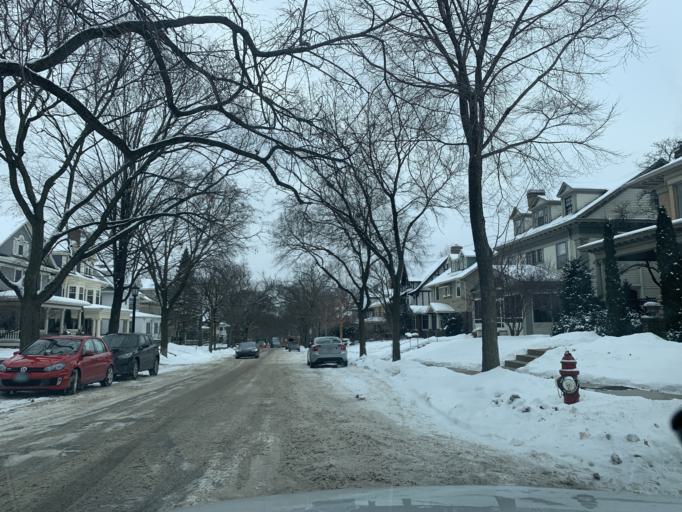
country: US
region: Minnesota
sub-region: Hennepin County
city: Minneapolis
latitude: 44.9654
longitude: -93.2957
